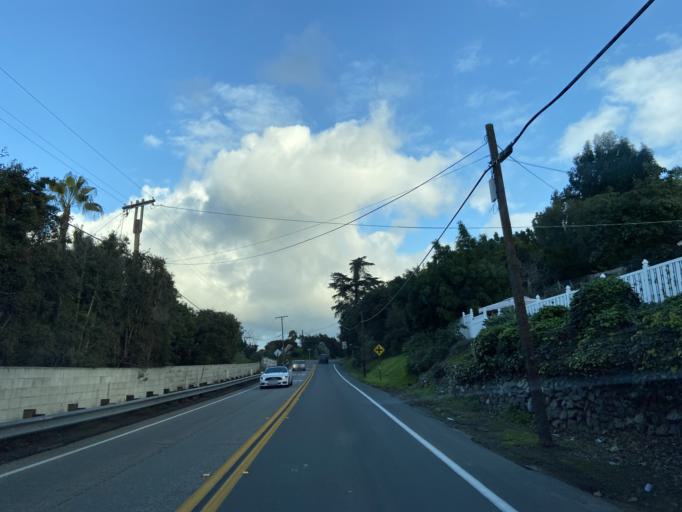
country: US
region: California
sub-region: San Diego County
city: Casa de Oro-Mount Helix
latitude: 32.7775
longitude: -116.9937
